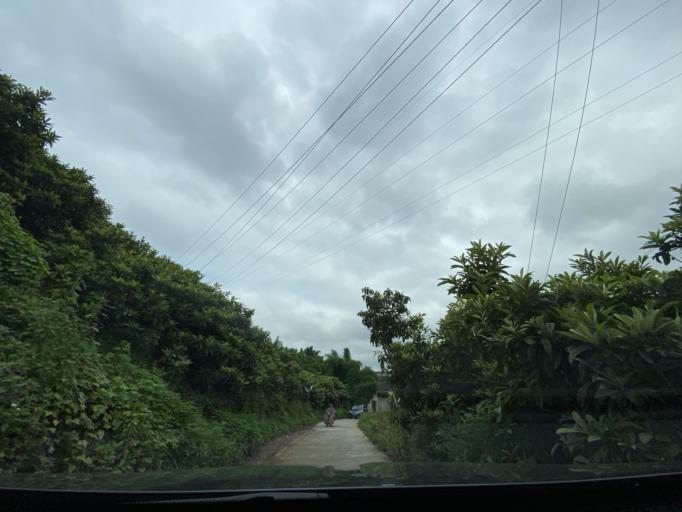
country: CN
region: Sichuan
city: Jiancheng
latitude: 30.3988
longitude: 104.5619
